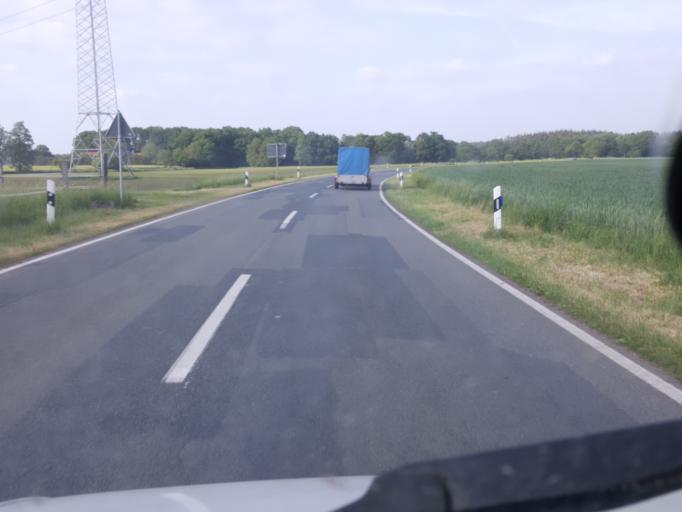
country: DE
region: Lower Saxony
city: Steyerberg
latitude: 52.5516
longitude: 8.9908
